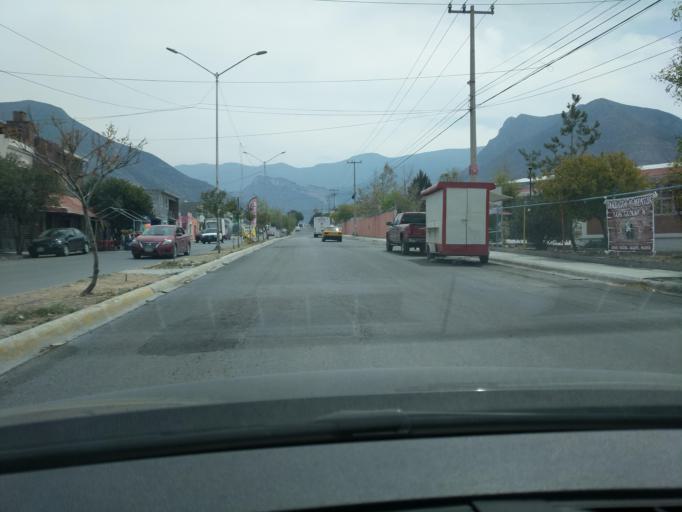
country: MX
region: Coahuila
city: Saltillo
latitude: 25.3519
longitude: -101.0131
